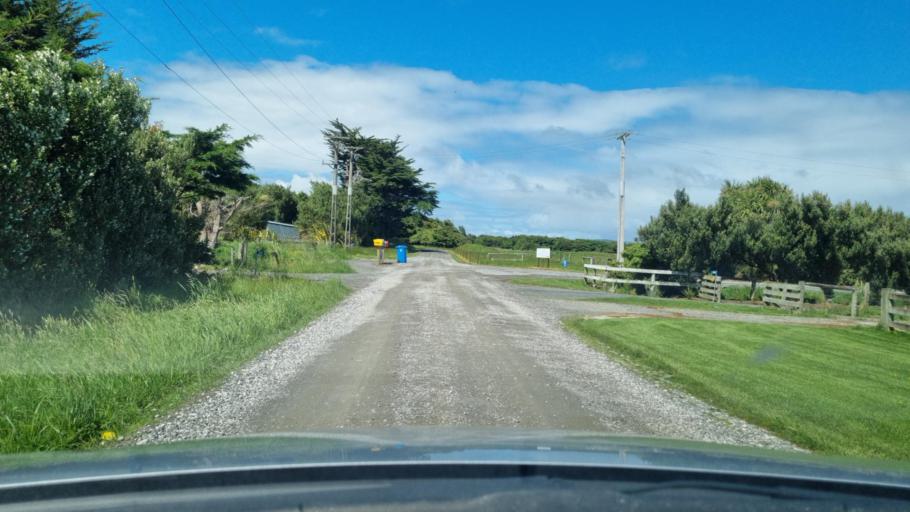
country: NZ
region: Southland
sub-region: Invercargill City
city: Invercargill
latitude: -46.4440
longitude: 168.2784
